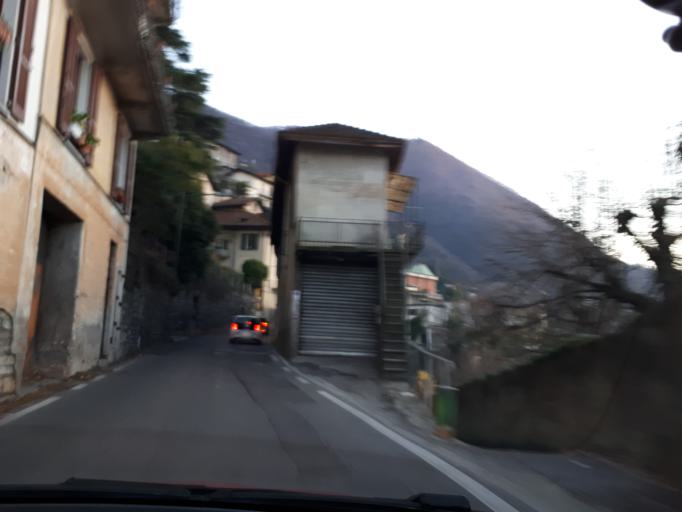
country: IT
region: Lombardy
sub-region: Provincia di Como
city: Blevio
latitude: 45.8414
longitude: 9.1042
